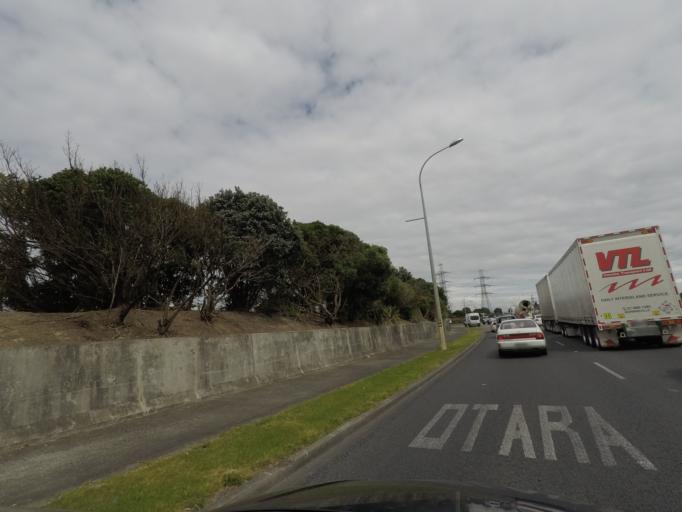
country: NZ
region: Auckland
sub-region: Auckland
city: Manukau City
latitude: -36.9504
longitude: 174.8598
